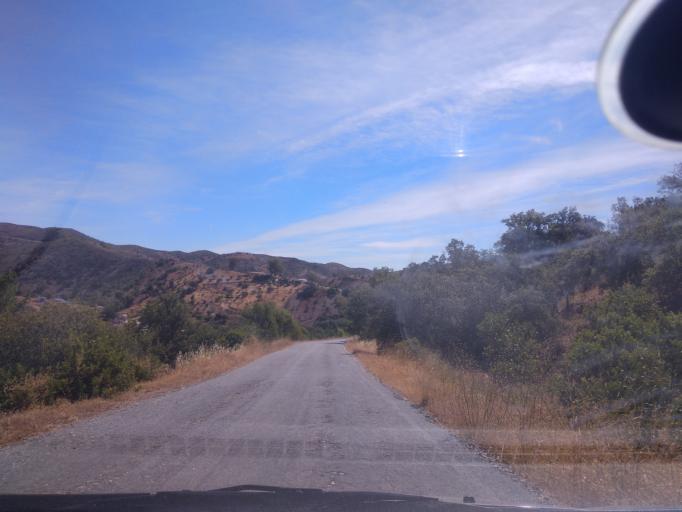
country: PT
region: Faro
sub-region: Sao Bras de Alportel
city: Sao Bras de Alportel
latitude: 37.1779
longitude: -7.8063
